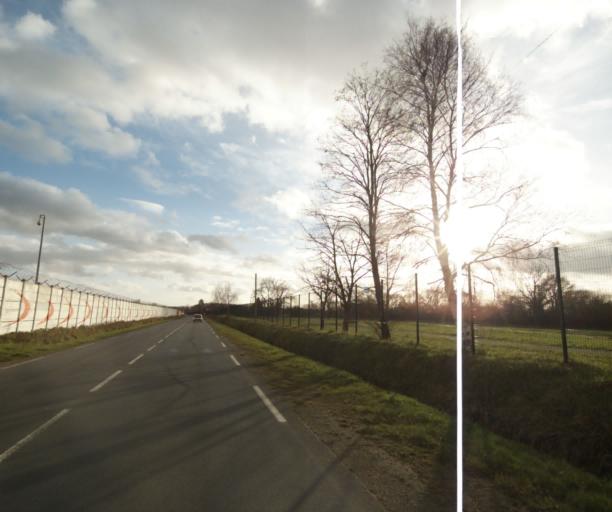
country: FR
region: Pays de la Loire
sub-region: Departement de la Sarthe
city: Arnage
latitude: 47.9431
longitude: 0.2075
